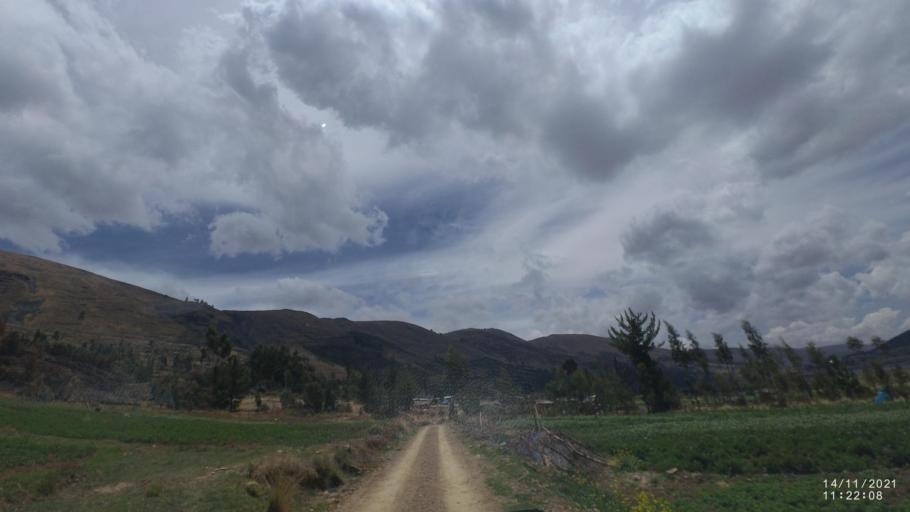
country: BO
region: Cochabamba
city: Cochabamba
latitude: -17.3359
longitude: -66.0337
